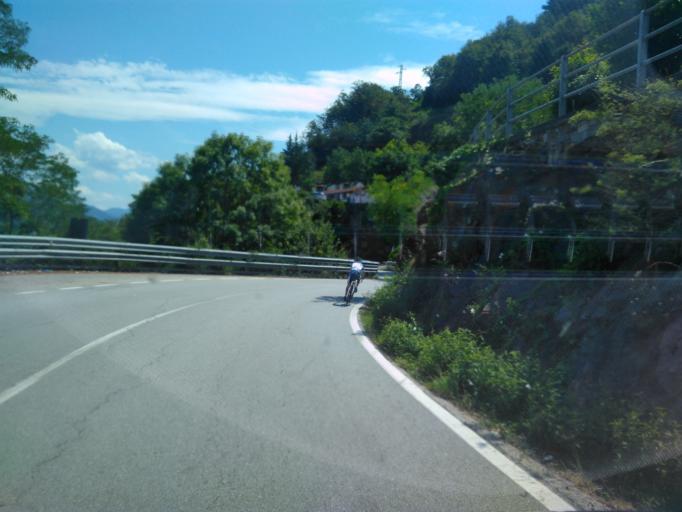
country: IT
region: Piedmont
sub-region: Provincia Verbano-Cusio-Ossola
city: Cannobio
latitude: 46.0777
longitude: 8.6935
